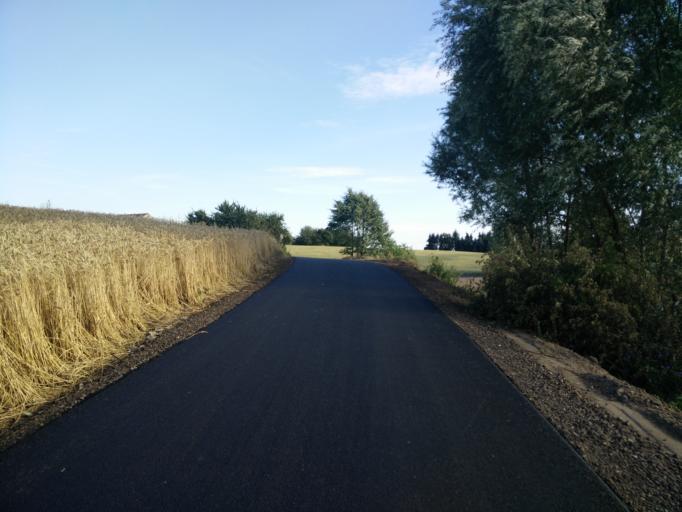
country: PL
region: Greater Poland Voivodeship
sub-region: Powiat sredzki
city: Sroda Wielkopolska
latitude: 52.2454
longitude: 17.2979
